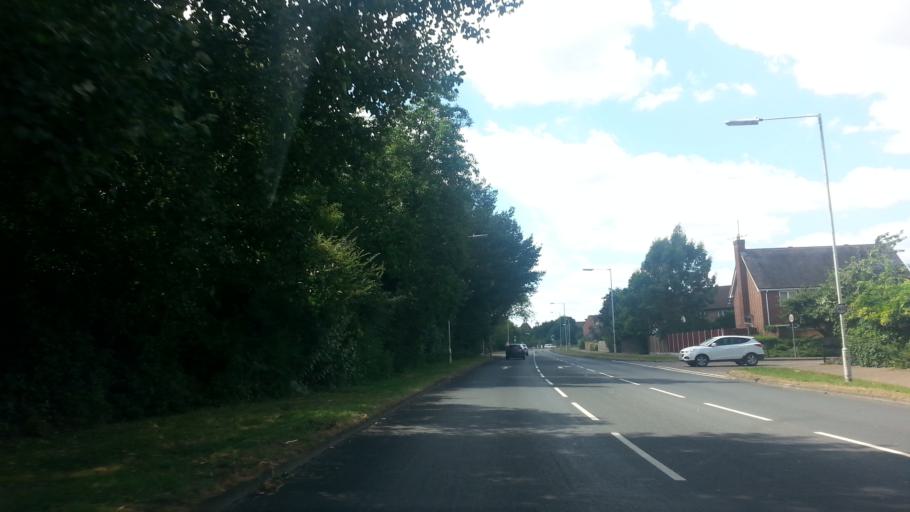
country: GB
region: England
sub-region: Essex
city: Chelmsford
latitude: 51.7315
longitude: 0.5004
